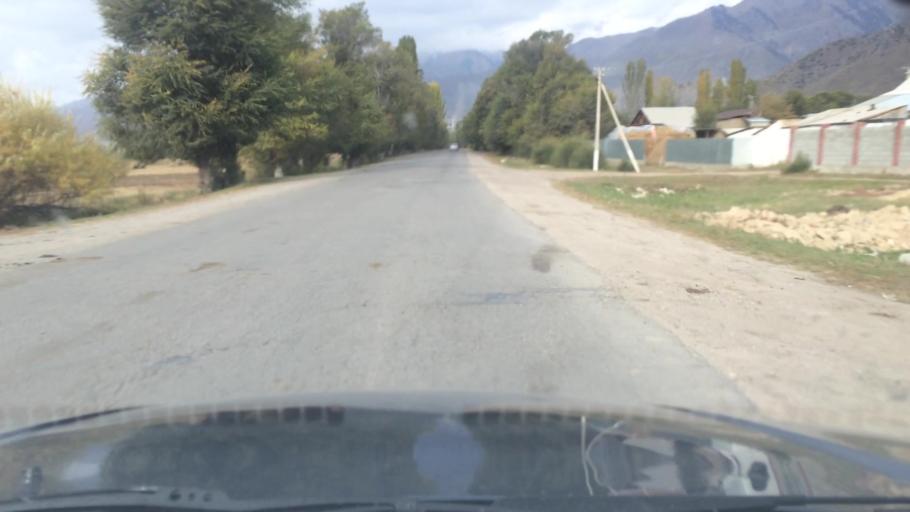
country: KG
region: Ysyk-Koel
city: Tyup
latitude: 42.7826
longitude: 78.2820
